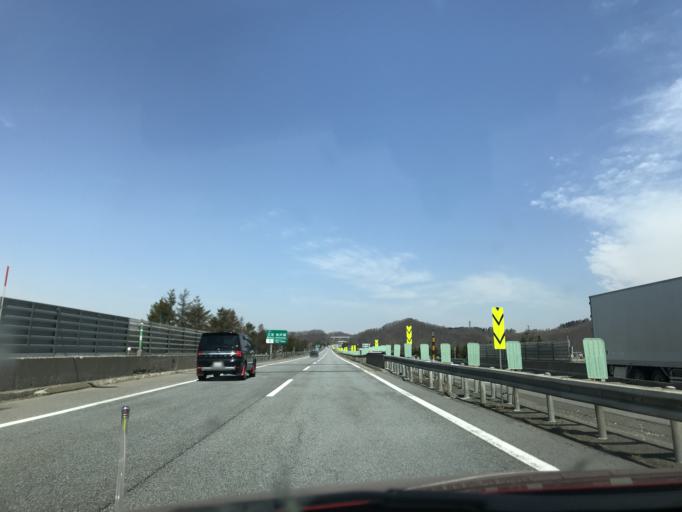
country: JP
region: Hokkaido
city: Iwamizawa
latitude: 43.2324
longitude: 141.8305
